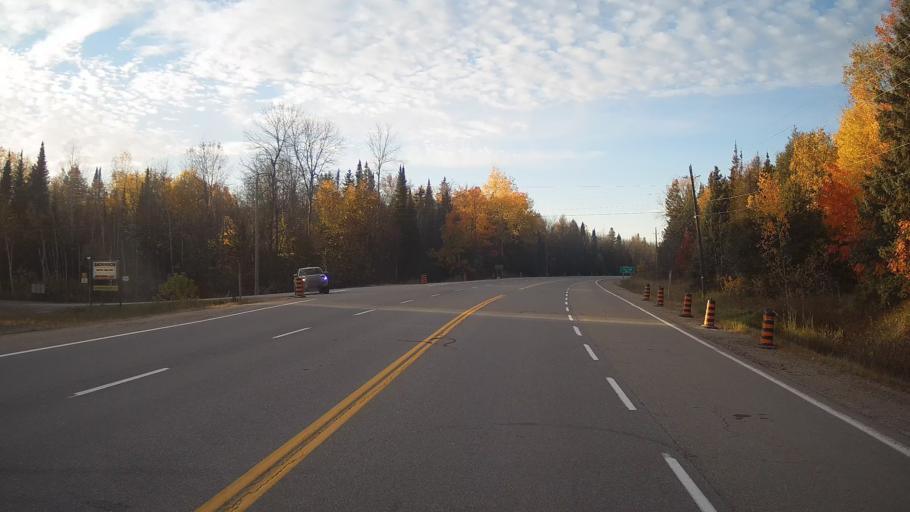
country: CA
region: Ontario
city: Perth
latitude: 45.0297
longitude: -76.2438
